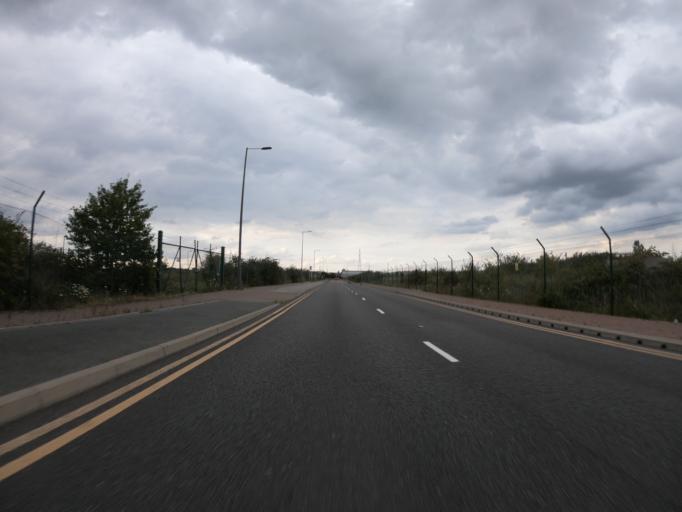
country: GB
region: England
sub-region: Greater London
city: Barking
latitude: 51.5122
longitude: 0.0808
